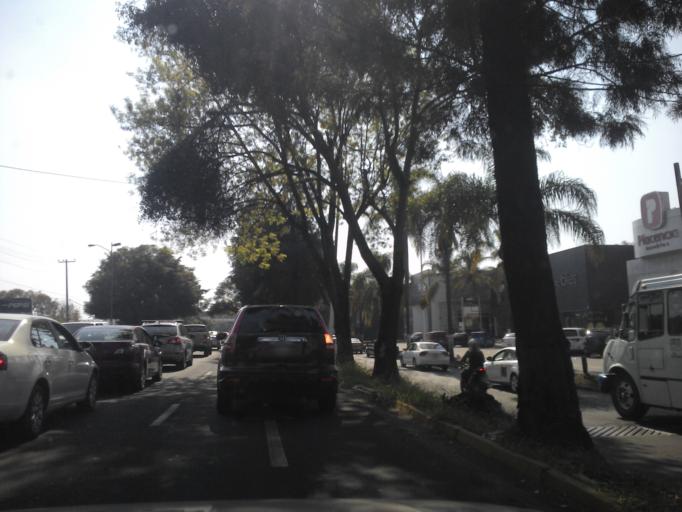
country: MX
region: Jalisco
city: Guadalajara
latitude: 20.6556
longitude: -103.4000
